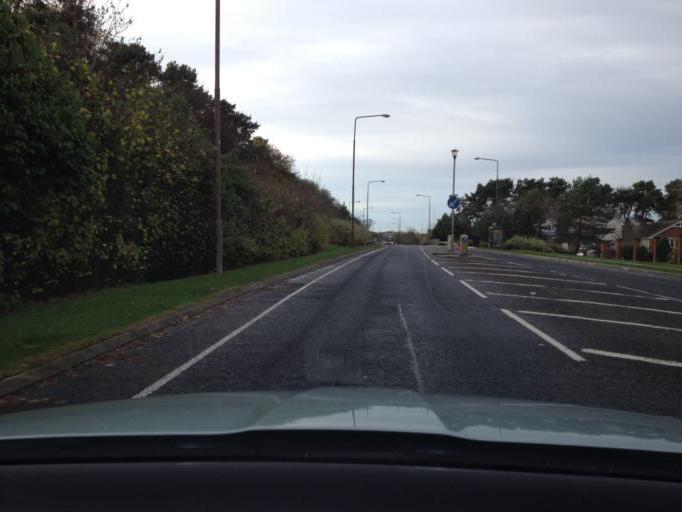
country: GB
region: Scotland
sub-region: West Lothian
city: Livingston
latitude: 55.8987
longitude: -3.5443
